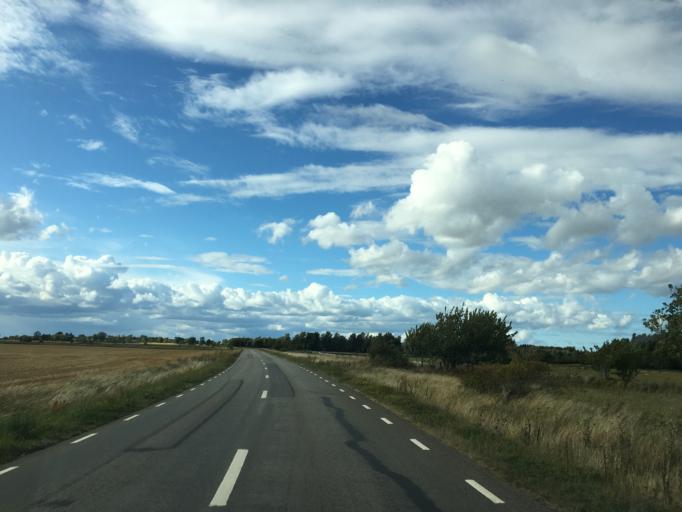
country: SE
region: Kalmar
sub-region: Morbylanga Kommun
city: Moerbylanga
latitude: 56.4333
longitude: 16.4359
